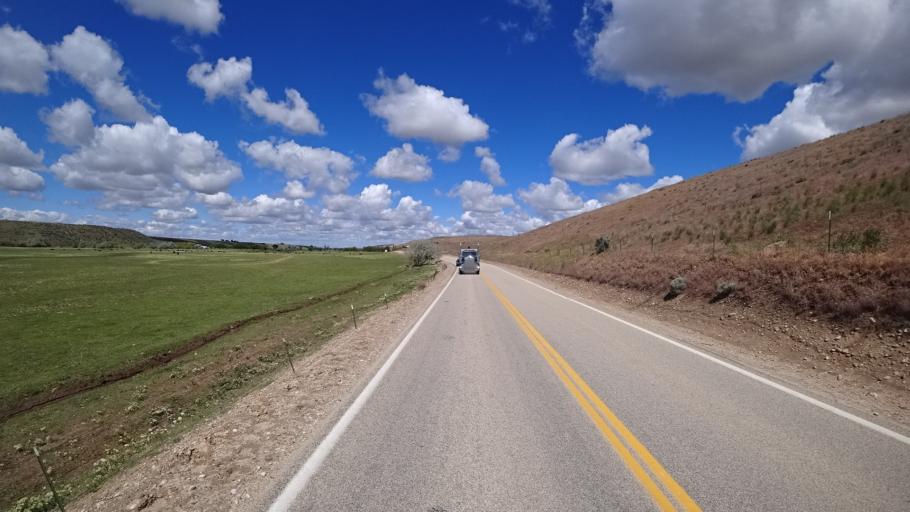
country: US
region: Idaho
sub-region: Ada County
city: Garden City
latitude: 43.4953
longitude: -116.2781
